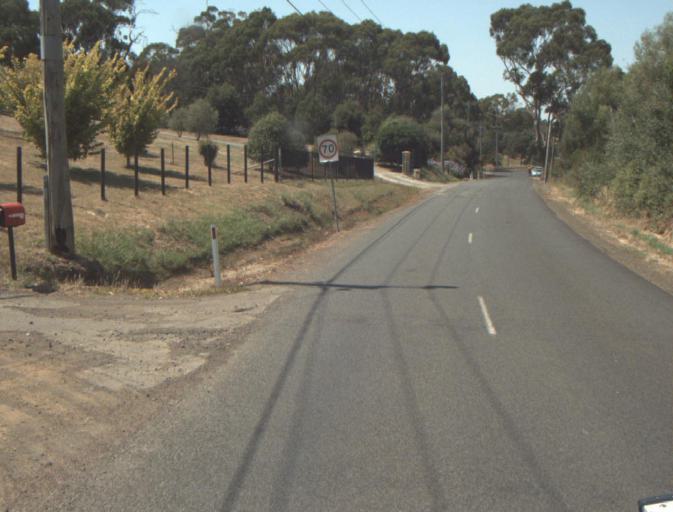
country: AU
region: Tasmania
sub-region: Launceston
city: Summerhill
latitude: -41.4930
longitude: 147.1798
